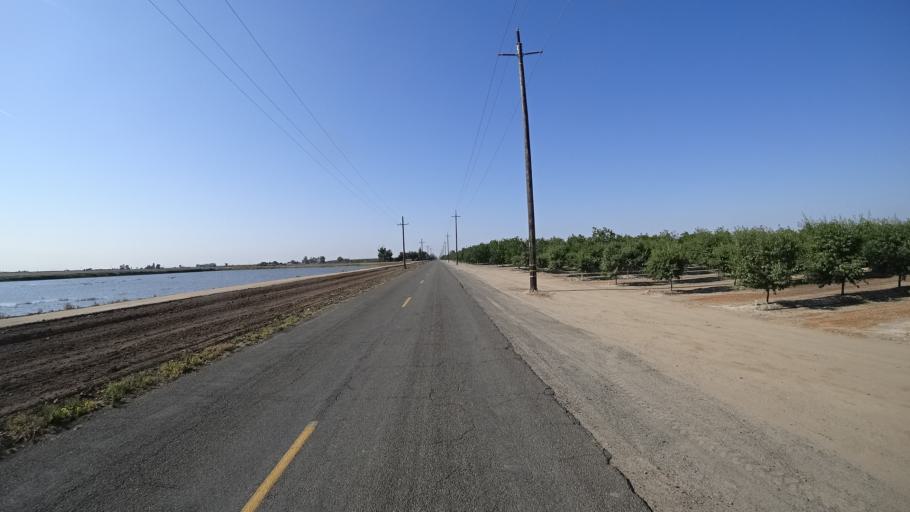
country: US
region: California
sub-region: Kings County
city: Home Garden
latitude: 36.3244
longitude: -119.5831
